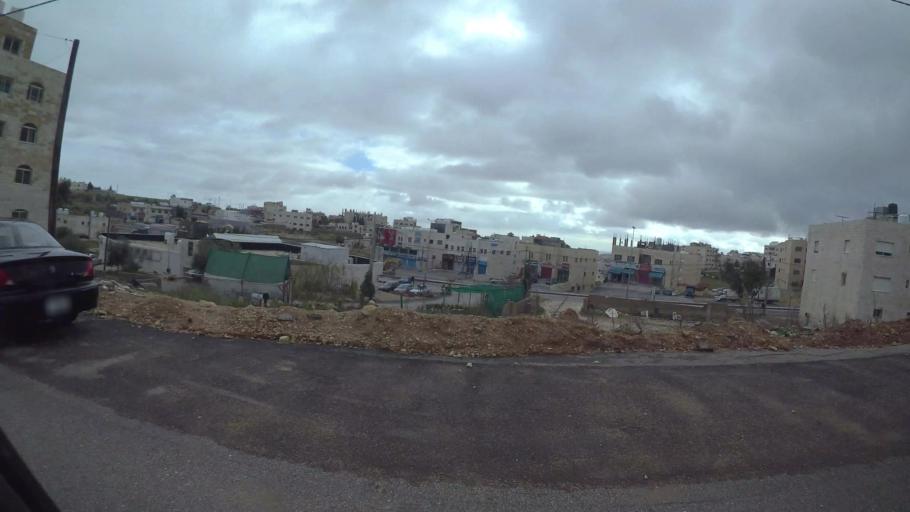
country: JO
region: Amman
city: Al Jubayhah
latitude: 32.0578
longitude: 35.8913
